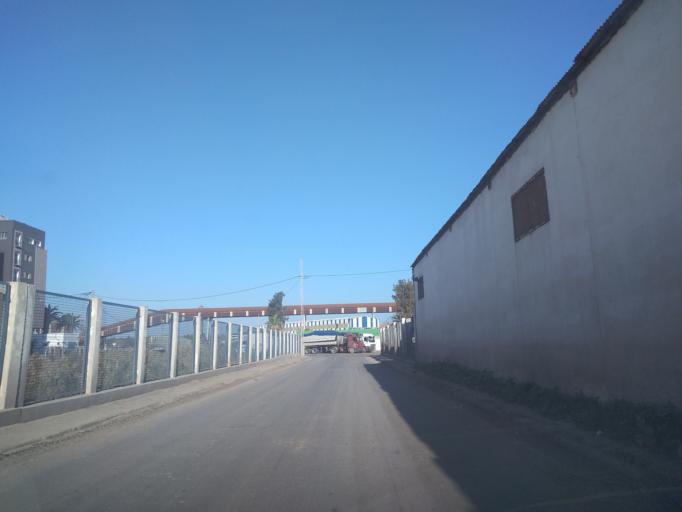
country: TN
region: Safaqis
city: Sfax
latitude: 34.7314
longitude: 10.7682
